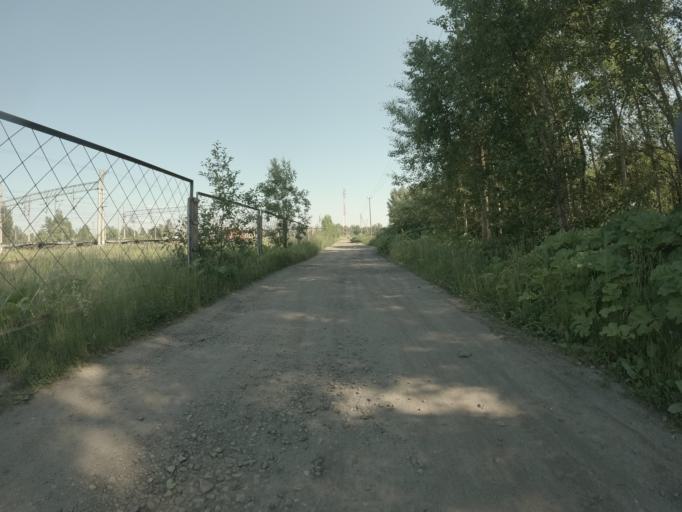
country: RU
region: Leningrad
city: Yakovlevo
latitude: 60.4689
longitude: 29.2809
